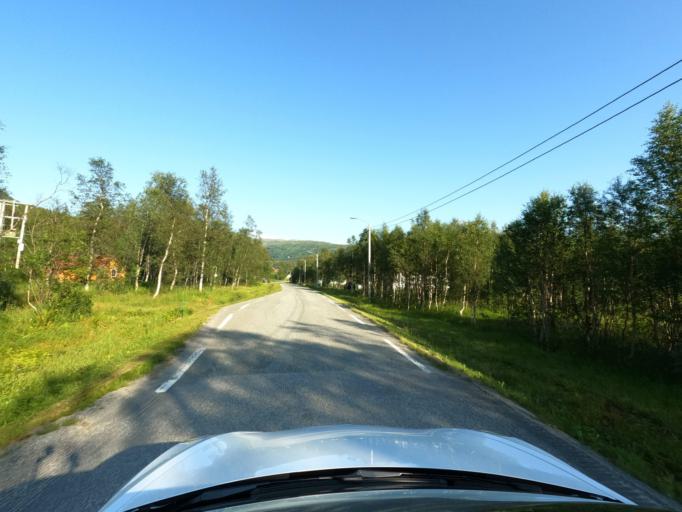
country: NO
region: Troms
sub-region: Gratangen
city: Gratangen
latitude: 68.5603
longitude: 17.7104
